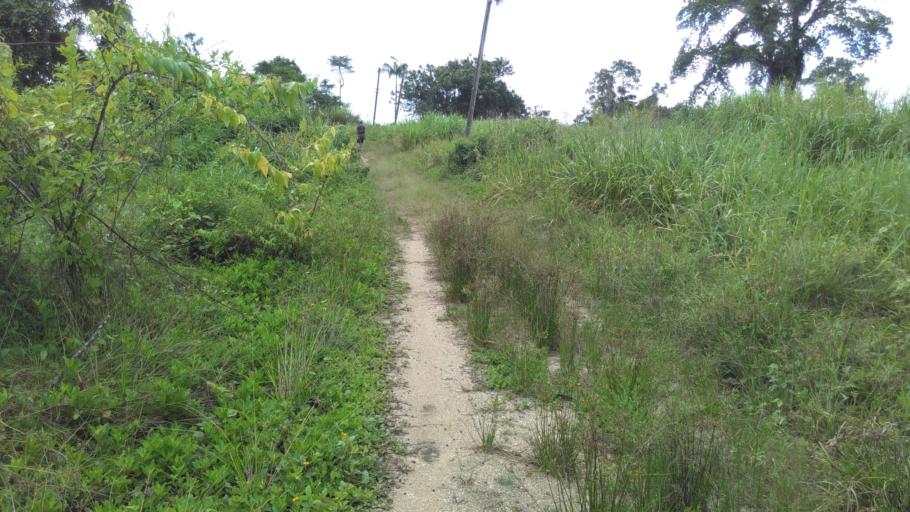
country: SR
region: Paramaribo
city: Paramaribo
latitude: 5.7739
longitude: -55.1302
